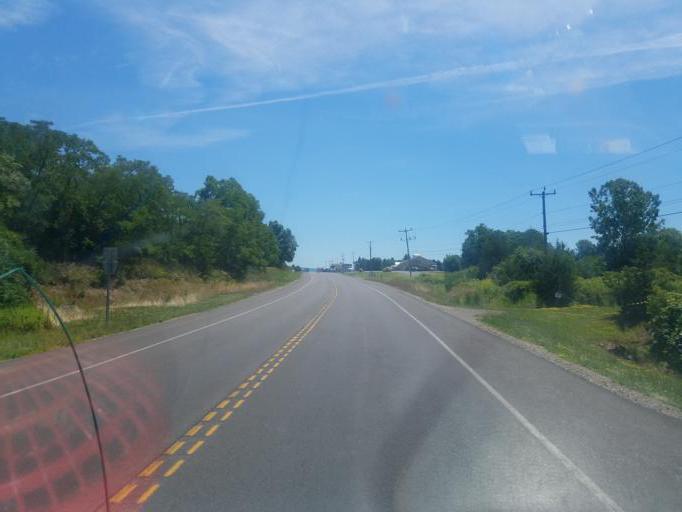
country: US
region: New York
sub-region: Yates County
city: Dundee
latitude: 42.5925
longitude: -76.9425
